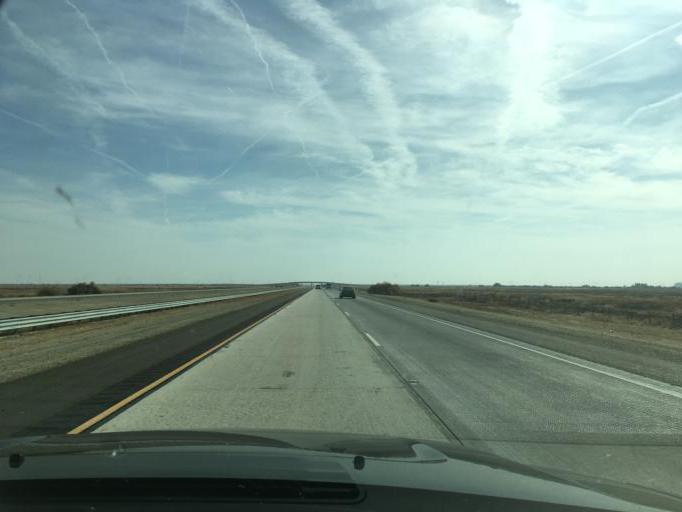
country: US
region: California
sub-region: Kern County
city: Lost Hills
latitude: 35.5670
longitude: -119.6080
